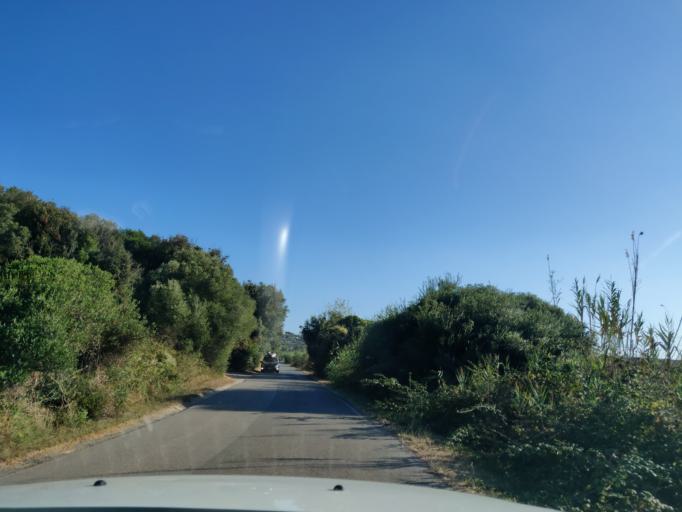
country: IT
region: Tuscany
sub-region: Provincia di Grosseto
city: Orbetello Scalo
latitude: 42.4263
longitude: 11.2816
